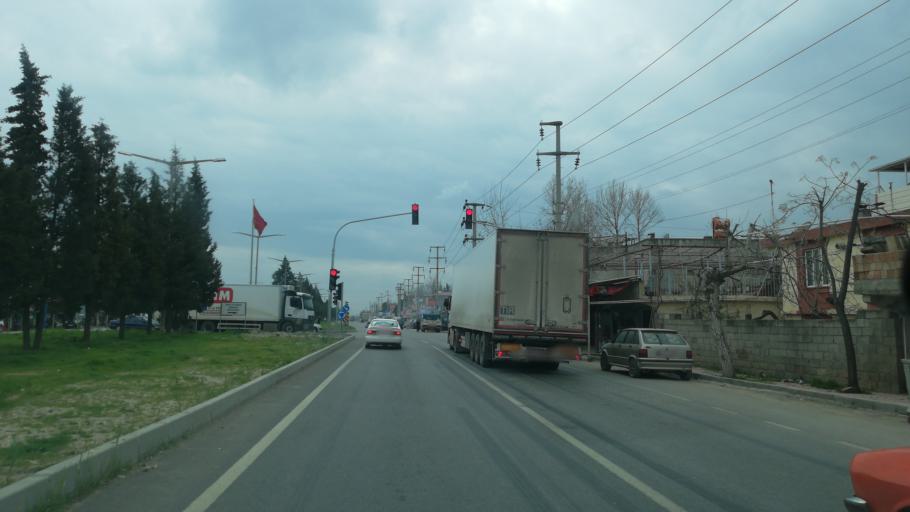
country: TR
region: Kahramanmaras
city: Turkoglu
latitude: 37.4130
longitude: 36.8795
